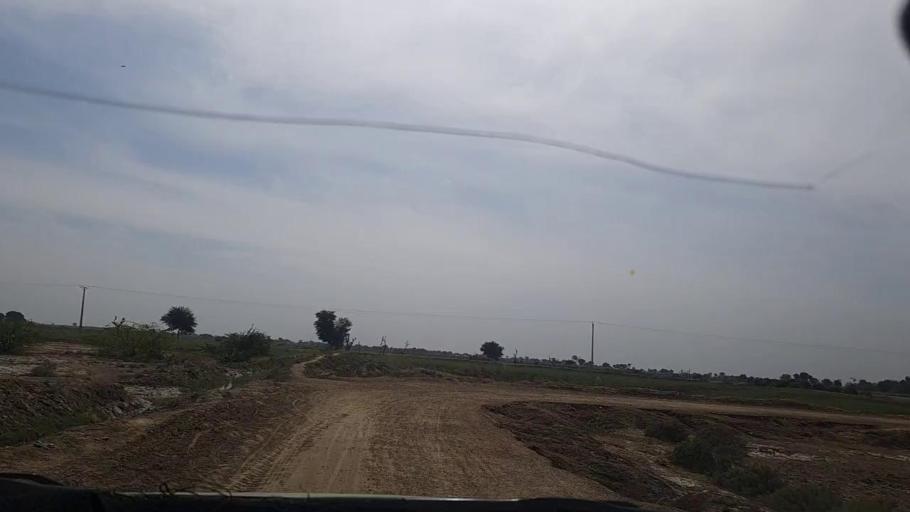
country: PK
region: Sindh
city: Dhoro Naro
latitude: 25.4551
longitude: 69.4747
